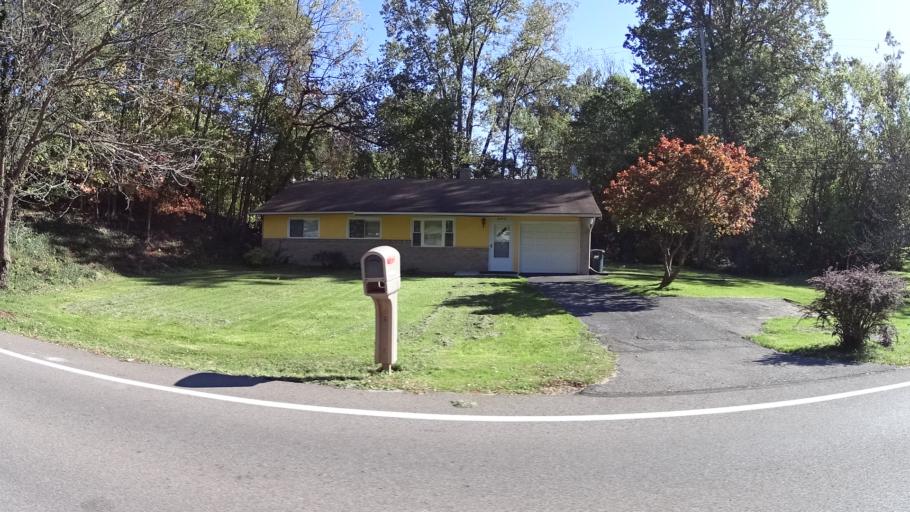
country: US
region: Ohio
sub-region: Lorain County
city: Amherst
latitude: 41.4177
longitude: -82.2254
